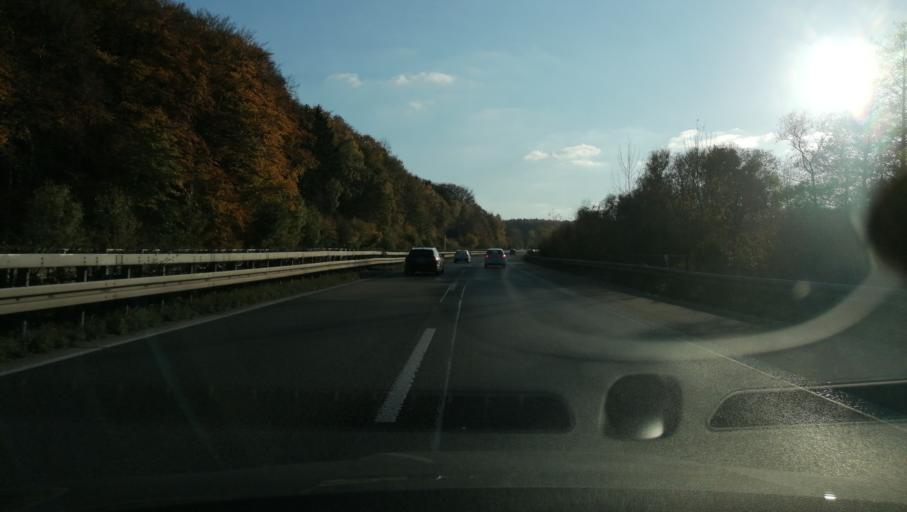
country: DE
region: North Rhine-Westphalia
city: Sprockhovel
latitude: 51.3459
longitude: 7.2746
